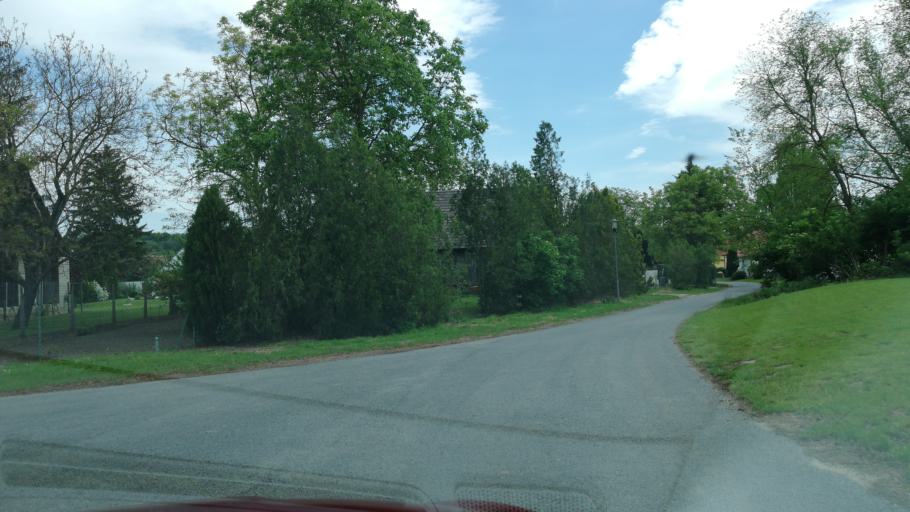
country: AT
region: Burgenland
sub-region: Politischer Bezirk Oberpullendorf
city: Lutzmannsburg
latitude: 47.4563
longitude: 16.6122
